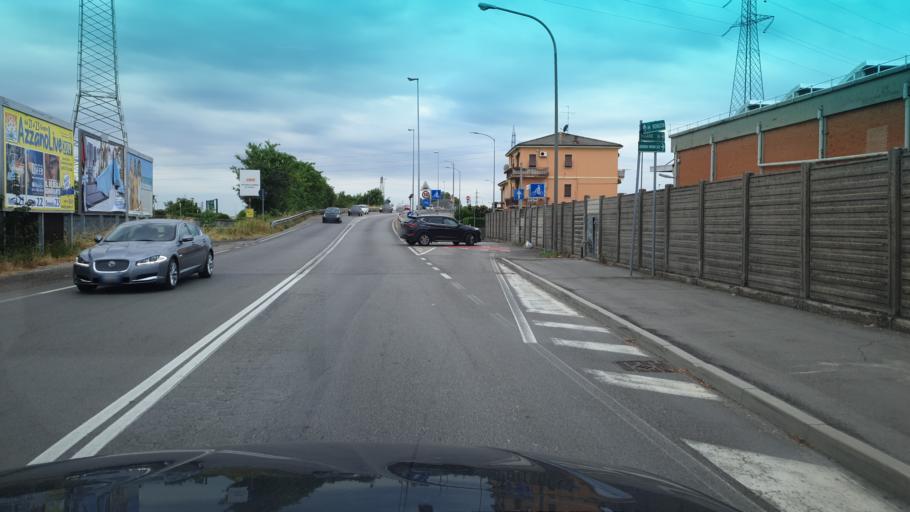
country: IT
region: Veneto
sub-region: Provincia di Verona
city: Beccacivetta-Azzano
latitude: 45.3989
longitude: 10.9805
